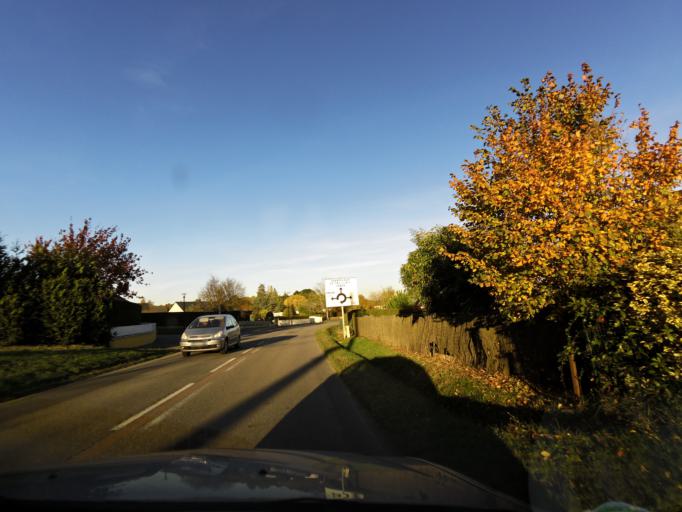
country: FR
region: Brittany
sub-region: Departement d'Ille-et-Vilaine
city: Crevin
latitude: 47.9352
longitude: -1.6560
